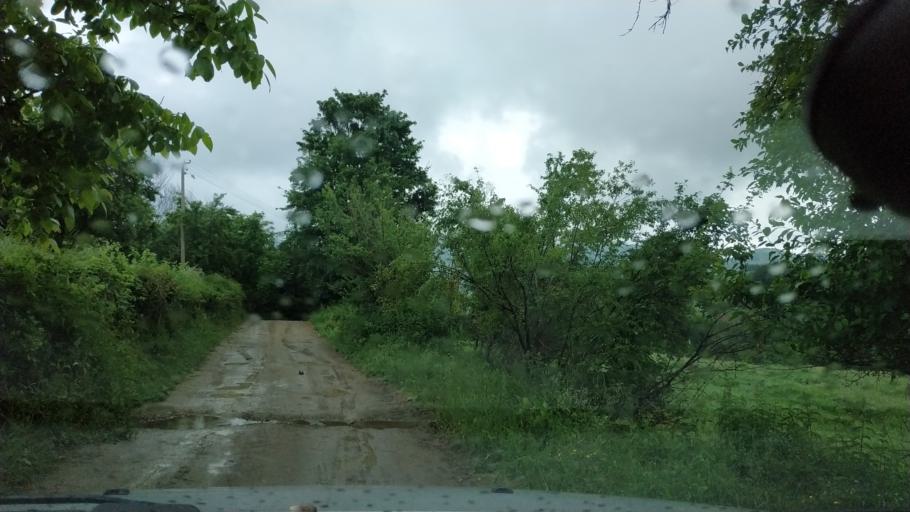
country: RS
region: Central Serbia
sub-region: Toplicki Okrug
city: Prokuplje
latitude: 43.4003
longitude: 21.5575
